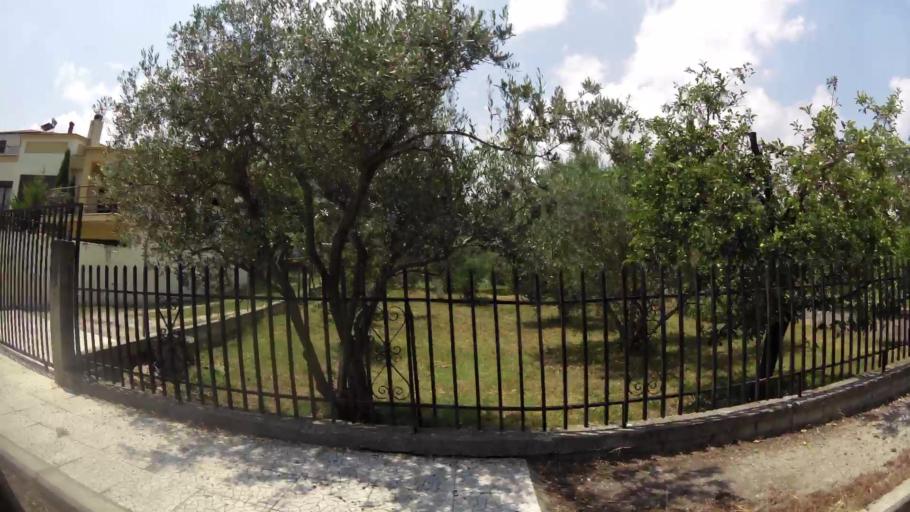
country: GR
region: Central Macedonia
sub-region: Nomos Imathias
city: Veroia
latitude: 40.5162
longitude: 22.1860
